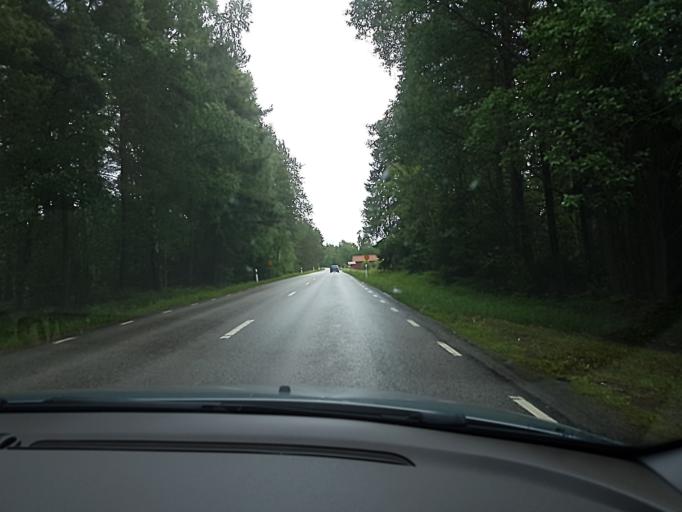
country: SE
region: Uppsala
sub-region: Osthammars Kommun
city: OEsthammar
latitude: 60.2782
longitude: 18.3009
